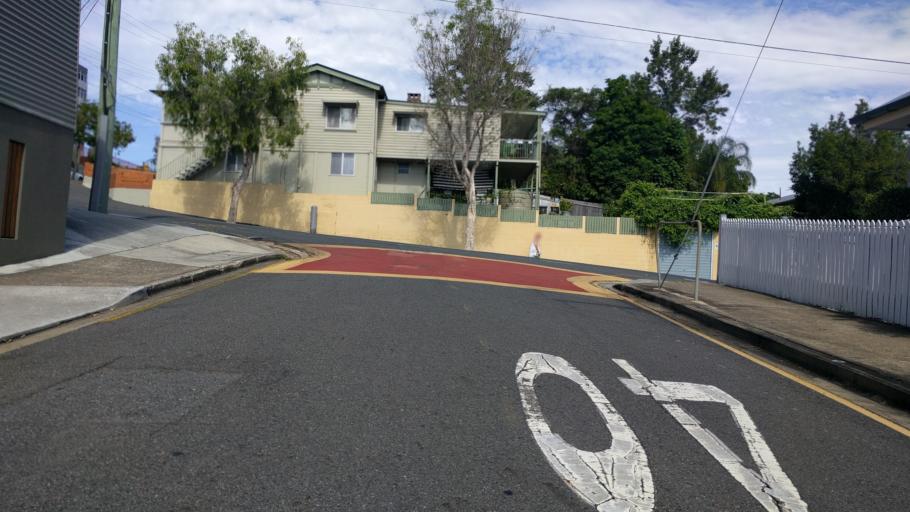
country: AU
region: Queensland
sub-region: Brisbane
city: South Brisbane
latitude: -27.4834
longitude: 153.0114
